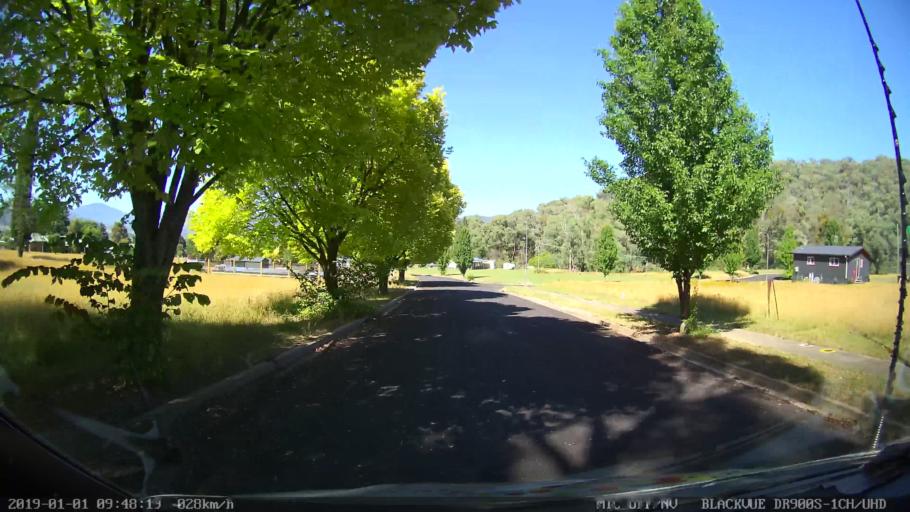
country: AU
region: New South Wales
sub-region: Snowy River
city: Jindabyne
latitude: -36.2115
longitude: 148.1329
